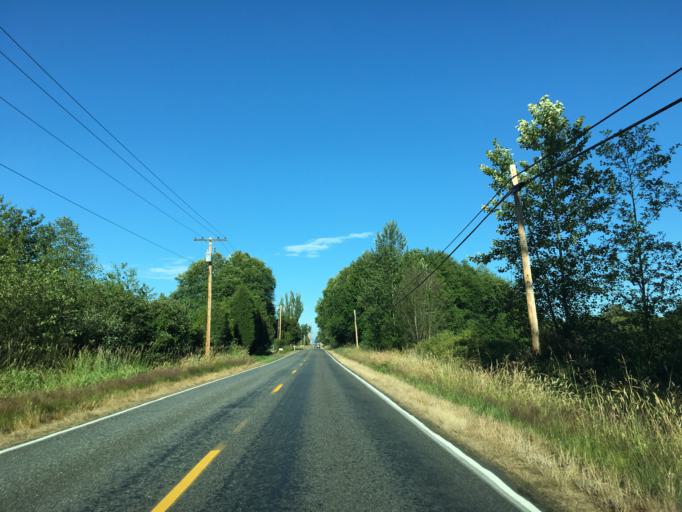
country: US
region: Washington
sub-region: Whatcom County
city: Birch Bay
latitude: 48.9068
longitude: -122.7349
